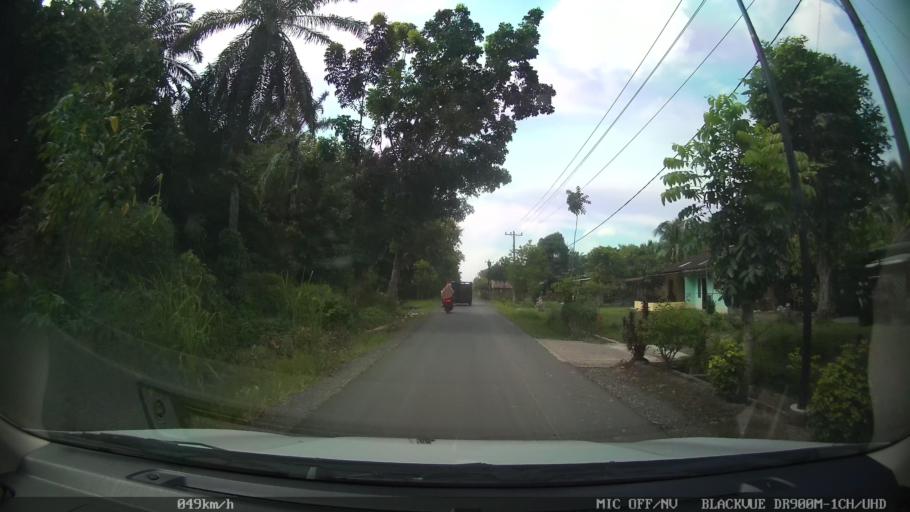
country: ID
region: North Sumatra
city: Binjai
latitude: 3.6482
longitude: 98.5178
